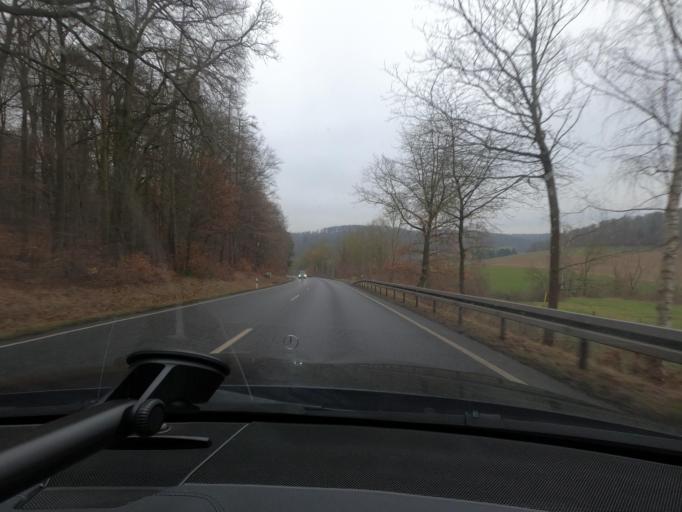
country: DE
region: Hesse
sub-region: Regierungsbezirk Kassel
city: Bad Arolsen
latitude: 51.3664
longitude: 9.0527
